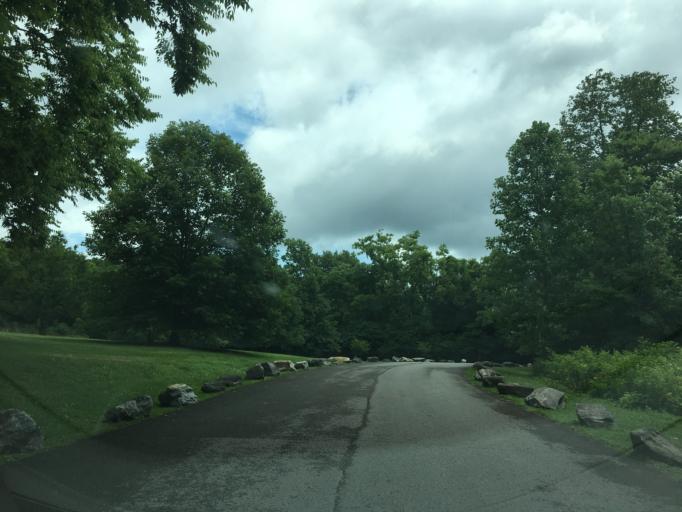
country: US
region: Tennessee
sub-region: Davidson County
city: Belle Meade
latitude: 36.0602
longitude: -86.9109
